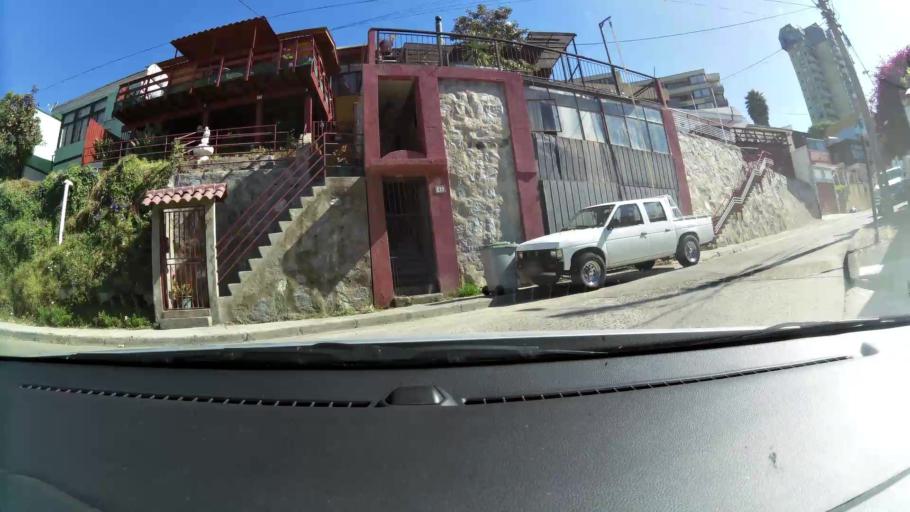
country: CL
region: Valparaiso
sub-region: Provincia de Valparaiso
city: Vina del Mar
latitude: -33.0346
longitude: -71.5656
